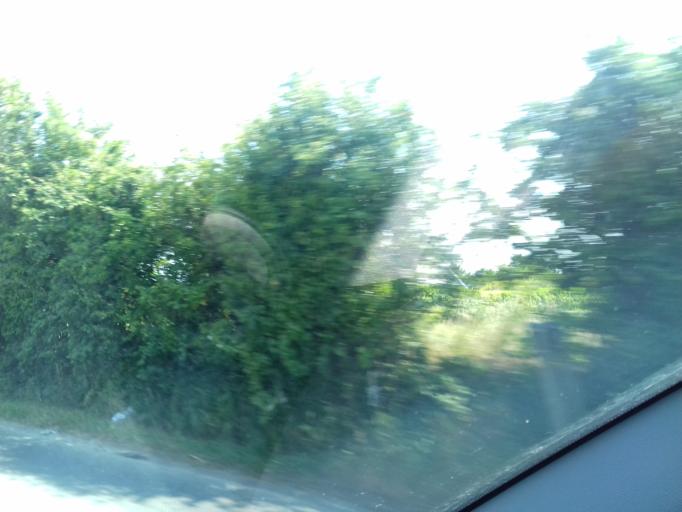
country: IE
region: Leinster
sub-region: An Mhi
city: Stamullin
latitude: 53.5977
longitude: -6.2431
